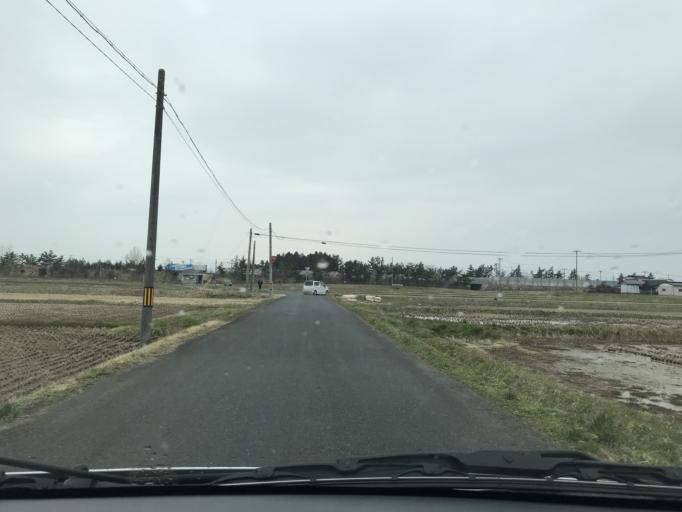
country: JP
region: Iwate
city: Mizusawa
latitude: 39.1305
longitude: 141.1221
